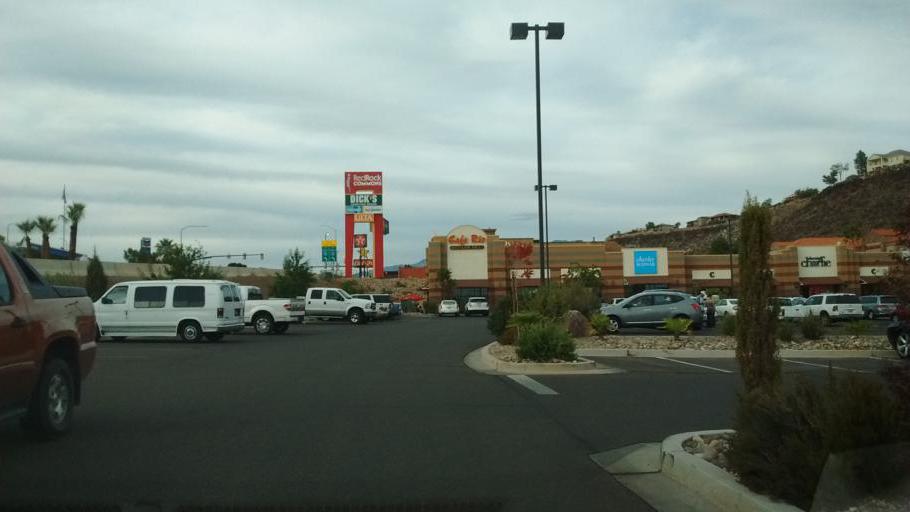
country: US
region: Utah
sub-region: Washington County
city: Saint George
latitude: 37.1080
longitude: -113.5544
